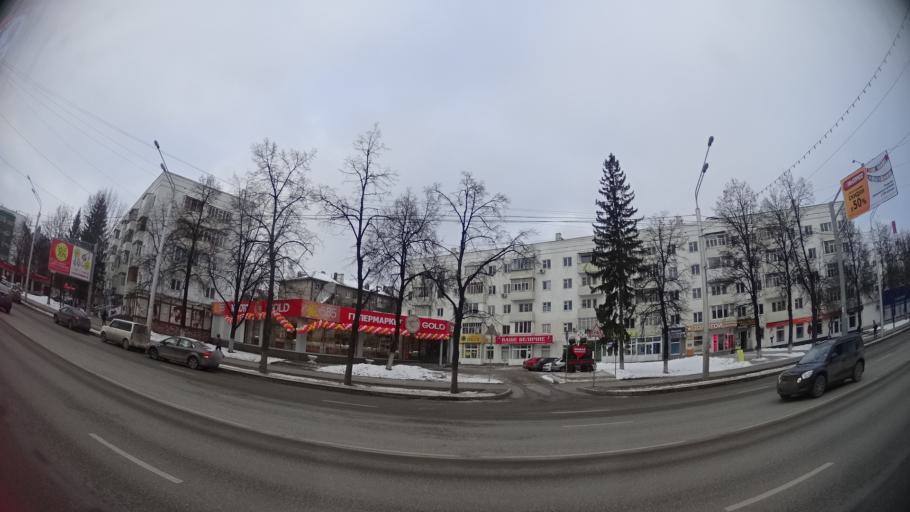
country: RU
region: Bashkortostan
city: Ufa
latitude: 54.7354
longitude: 55.9632
